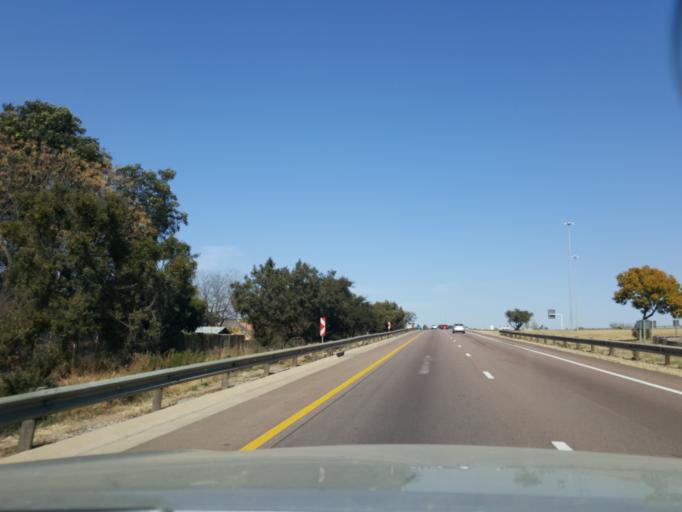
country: ZA
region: Gauteng
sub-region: City of Tshwane Metropolitan Municipality
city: Centurion
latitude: -25.8286
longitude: 28.2457
